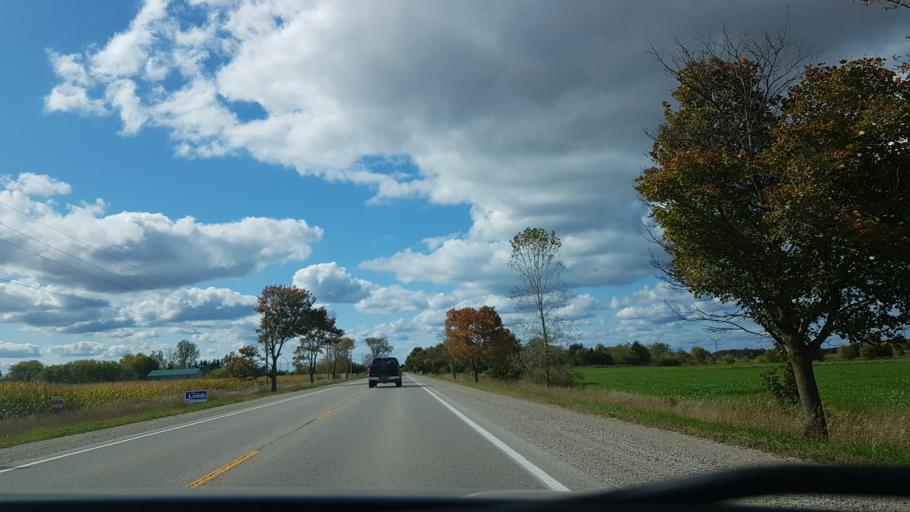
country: CA
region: Ontario
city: Bluewater
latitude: 43.3442
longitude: -81.6534
